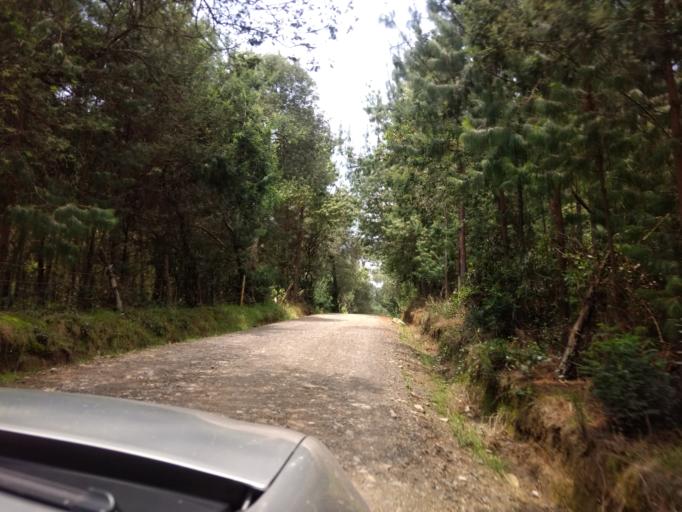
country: CO
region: Boyaca
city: Raquira
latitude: 5.5125
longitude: -73.7157
